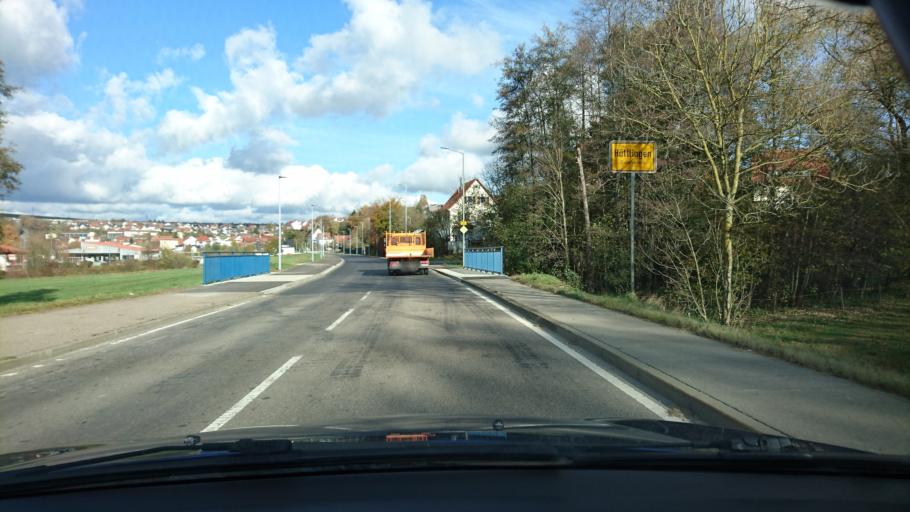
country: DE
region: Baden-Wuerttemberg
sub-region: Regierungsbezirk Stuttgart
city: Huttlingen
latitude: 48.8845
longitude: 10.0984
